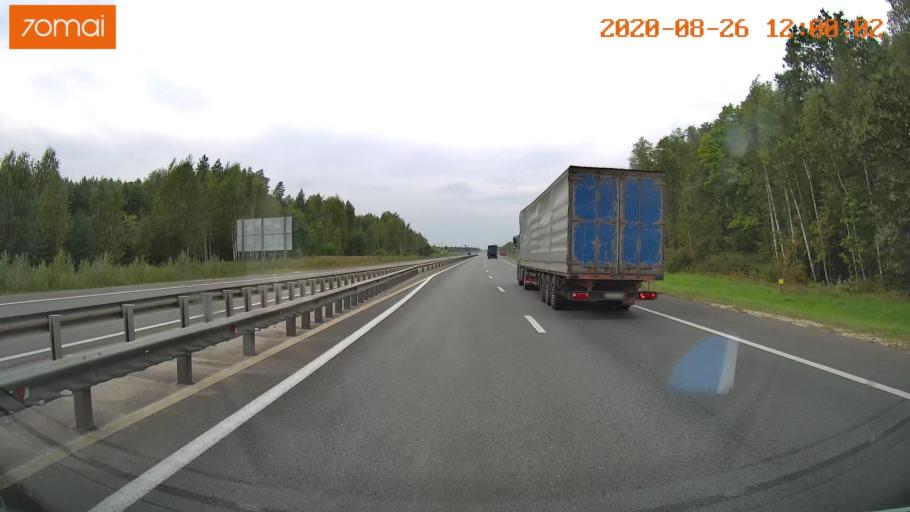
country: RU
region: Rjazan
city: Kiritsy
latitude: 54.2864
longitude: 40.2837
